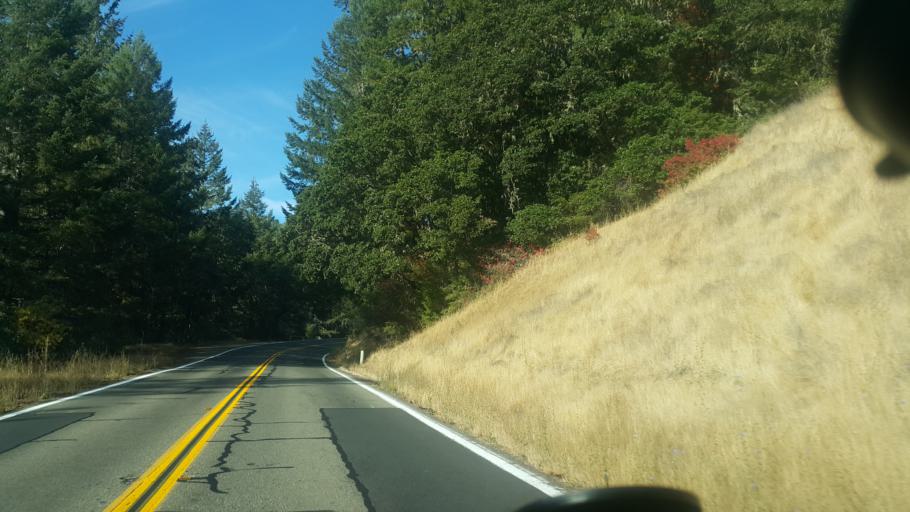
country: US
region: California
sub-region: Mendocino County
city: Brooktrails
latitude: 39.3885
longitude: -123.4233
